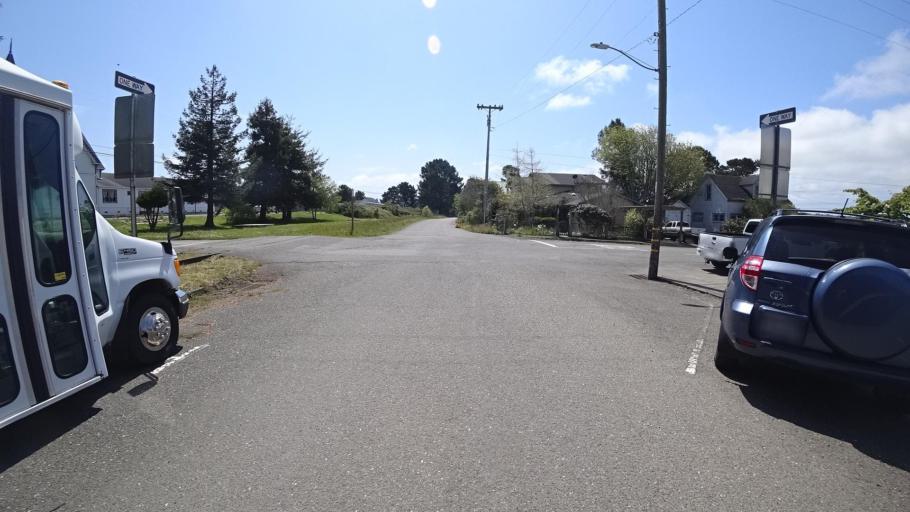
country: US
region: California
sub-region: Humboldt County
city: Ferndale
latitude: 40.6398
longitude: -124.2248
